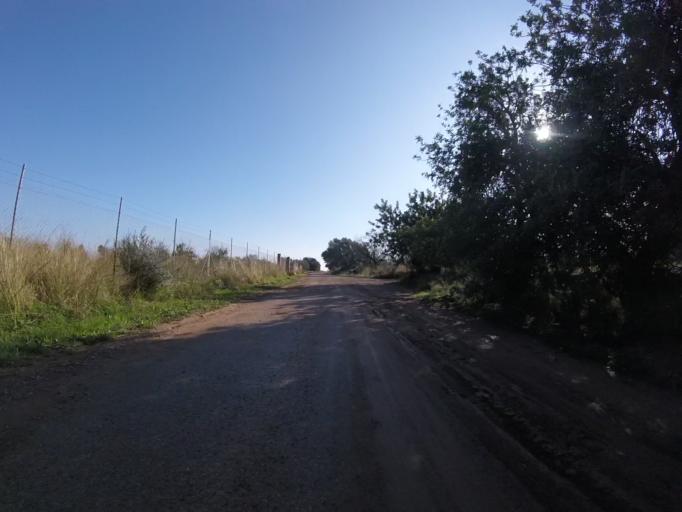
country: ES
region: Valencia
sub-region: Provincia de Castello
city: Peniscola
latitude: 40.3893
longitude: 0.3709
